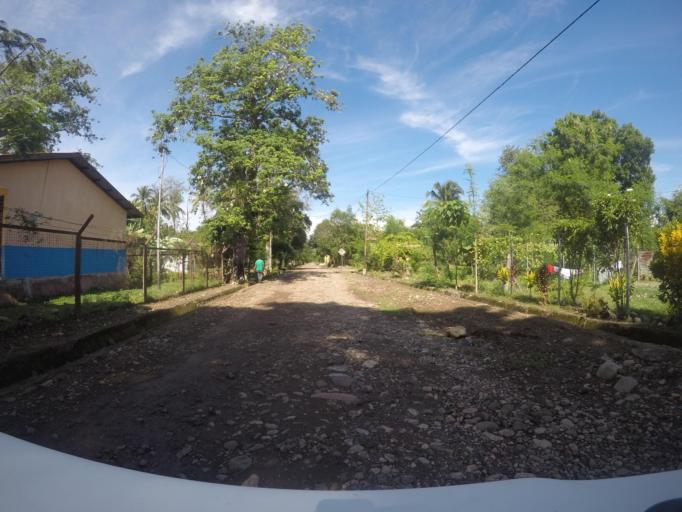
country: TL
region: Bobonaro
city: Maliana
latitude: -8.9877
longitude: 125.2013
